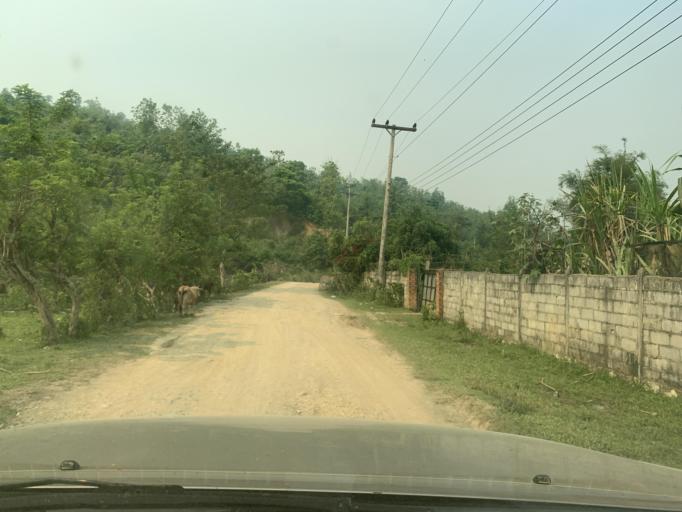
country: LA
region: Louangphabang
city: Louangphabang
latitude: 19.9029
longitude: 102.2545
